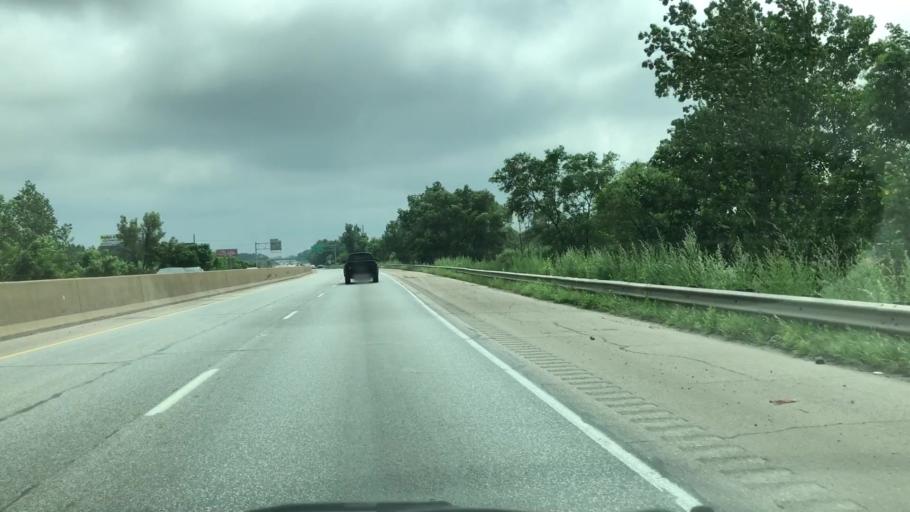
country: US
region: Indiana
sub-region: Lake County
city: East Chicago
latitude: 41.5980
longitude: -87.4328
